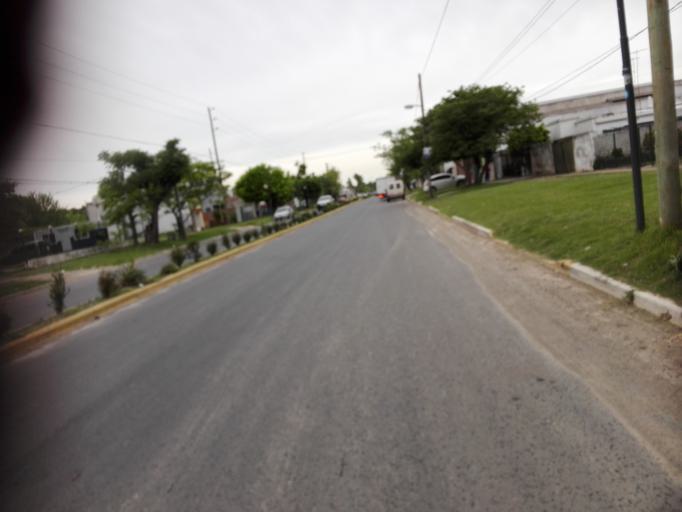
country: AR
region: Buenos Aires
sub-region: Partido de La Plata
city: La Plata
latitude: -34.9215
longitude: -57.9957
